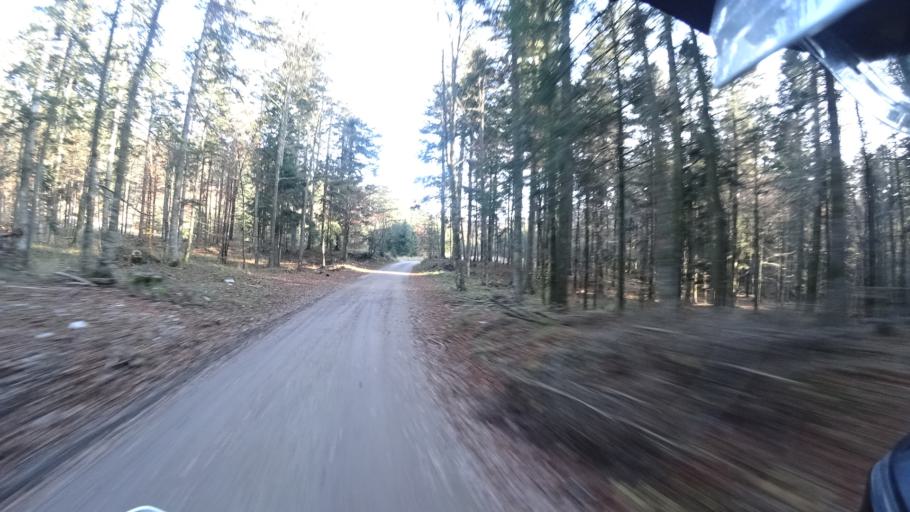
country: HR
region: Primorsko-Goranska
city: Klana
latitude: 45.4878
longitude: 14.4622
